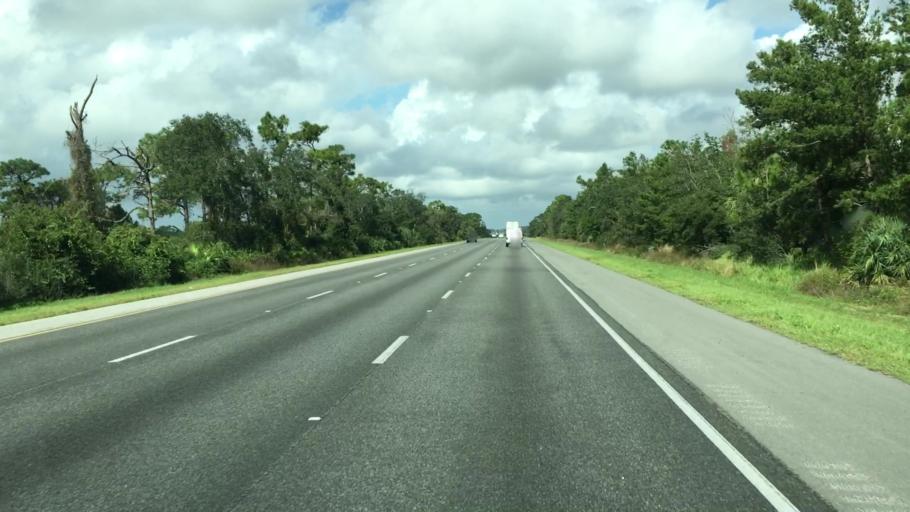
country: US
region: Florida
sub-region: Volusia County
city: Samsula-Spruce Creek
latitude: 29.0753
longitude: -81.0133
